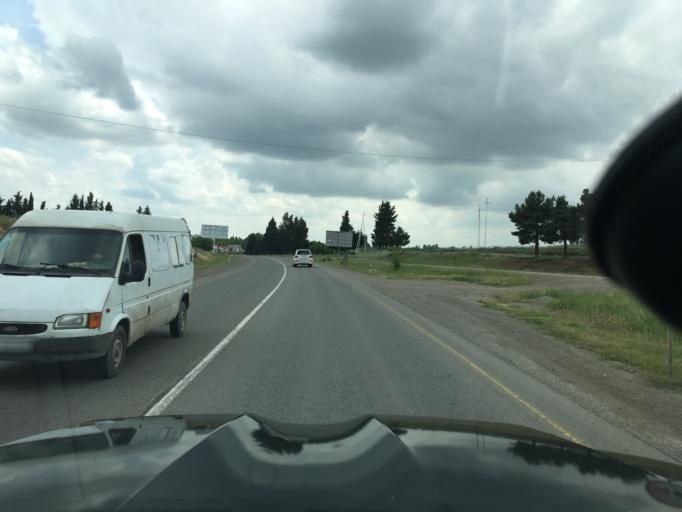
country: AZ
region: Tovuz
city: Tovuz
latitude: 40.9769
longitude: 45.6707
